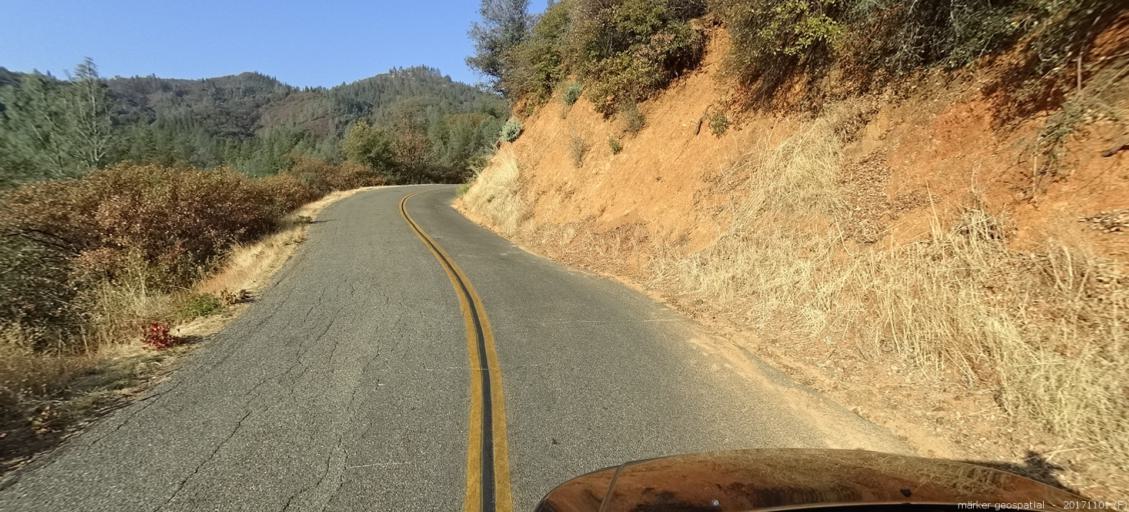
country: US
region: California
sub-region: Shasta County
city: Shasta Lake
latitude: 40.8039
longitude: -122.3172
